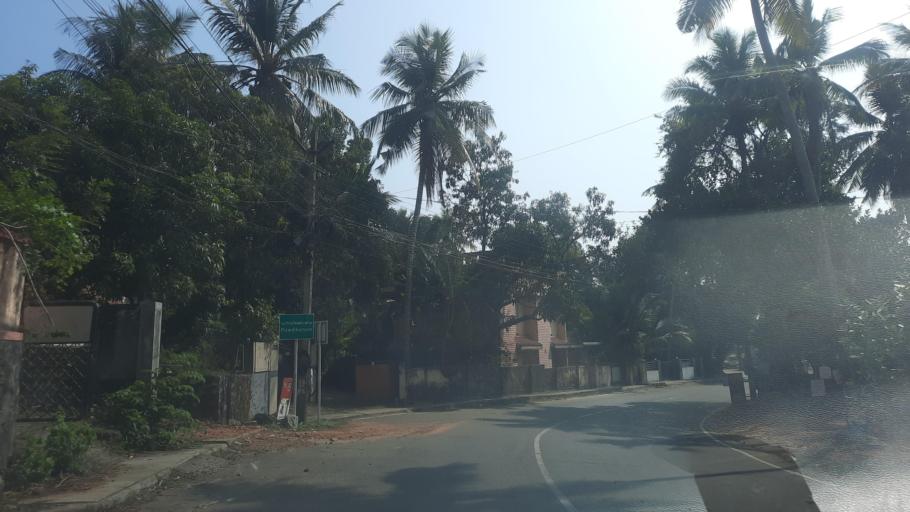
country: IN
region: Kerala
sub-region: Thiruvananthapuram
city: Nedumangad
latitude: 8.5779
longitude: 76.9261
